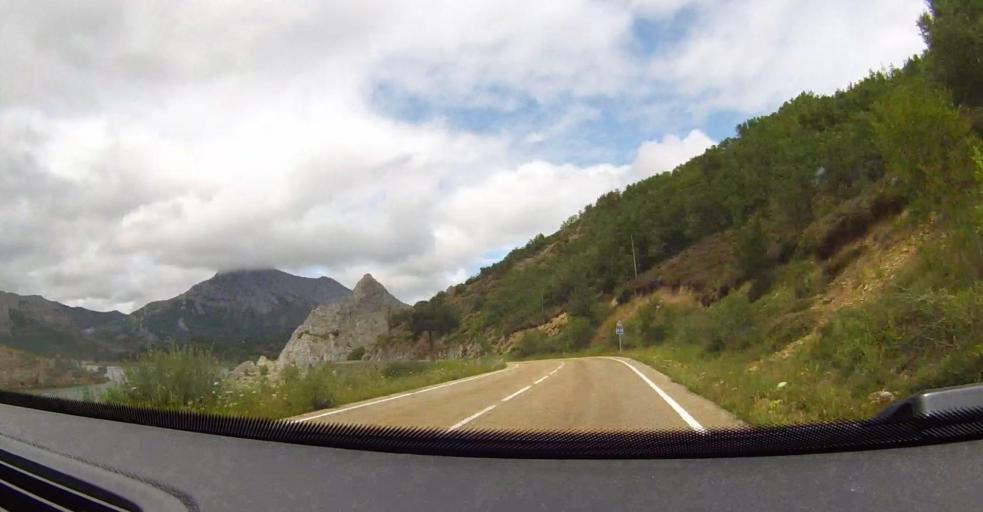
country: ES
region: Castille and Leon
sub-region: Provincia de Leon
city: Reyero
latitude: 42.9559
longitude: -5.2499
